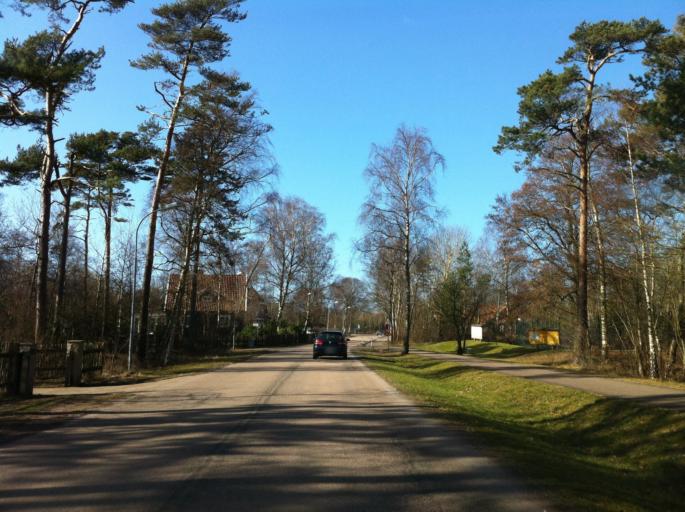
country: SE
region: Skane
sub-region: Angelholms Kommun
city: AEngelholm
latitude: 56.2596
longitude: 12.8393
